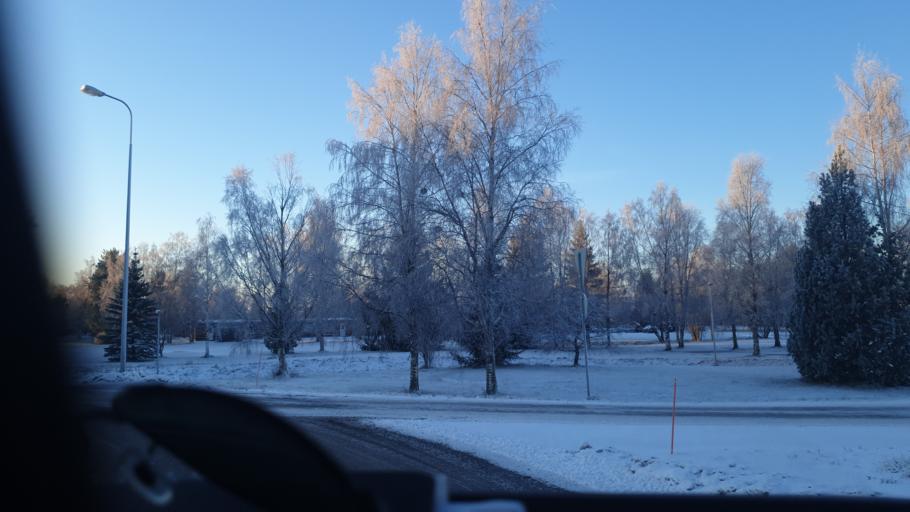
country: FI
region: Northern Ostrobothnia
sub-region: Ylivieska
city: Kalajoki
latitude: 64.2611
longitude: 23.9469
